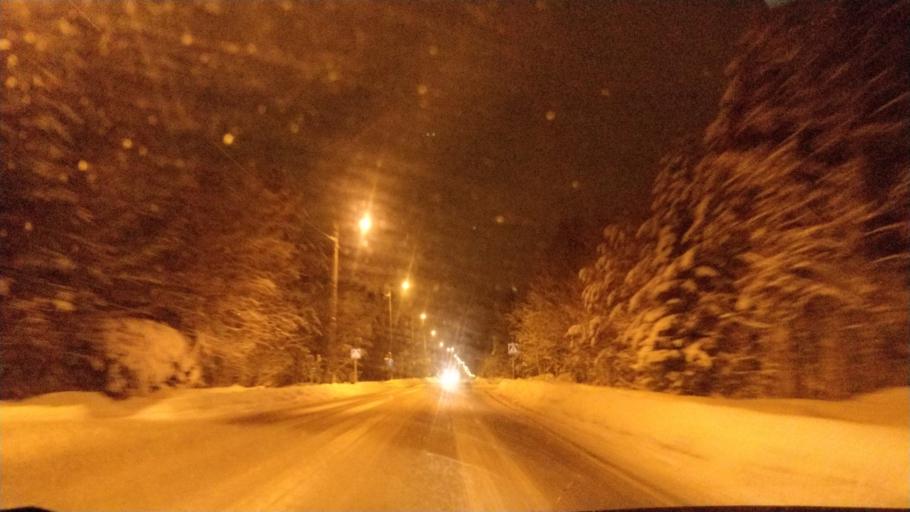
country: FI
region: Lapland
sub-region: Rovaniemi
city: Rovaniemi
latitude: 66.3733
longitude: 25.3821
